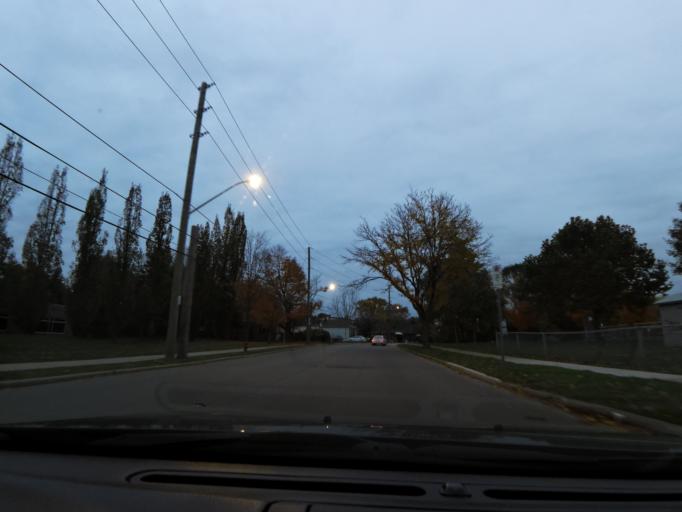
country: CA
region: Ontario
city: Ancaster
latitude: 43.2532
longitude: -79.9271
